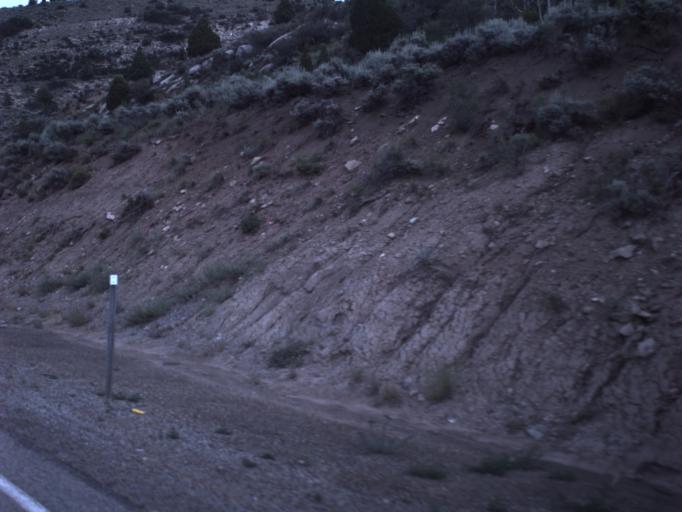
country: US
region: Utah
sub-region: Carbon County
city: Helper
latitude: 39.8316
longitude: -110.7867
